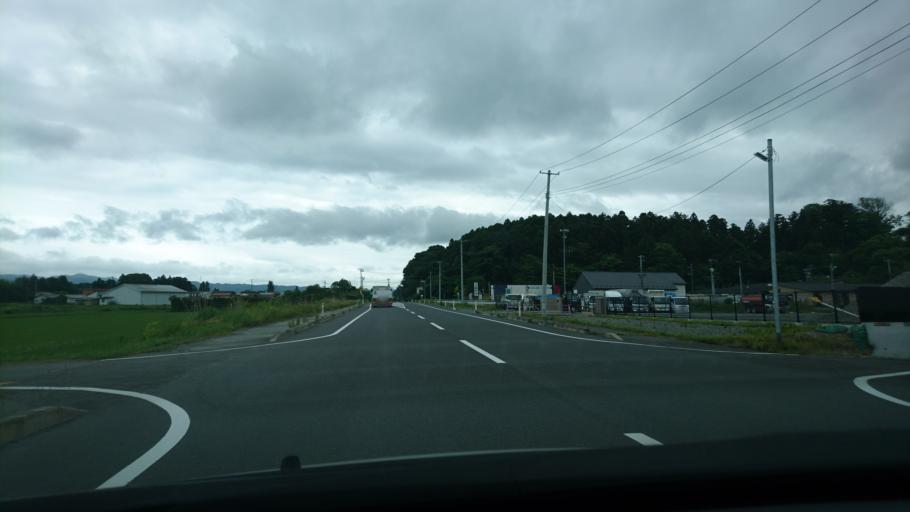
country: JP
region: Iwate
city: Ichinoseki
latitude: 38.7348
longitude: 141.2587
